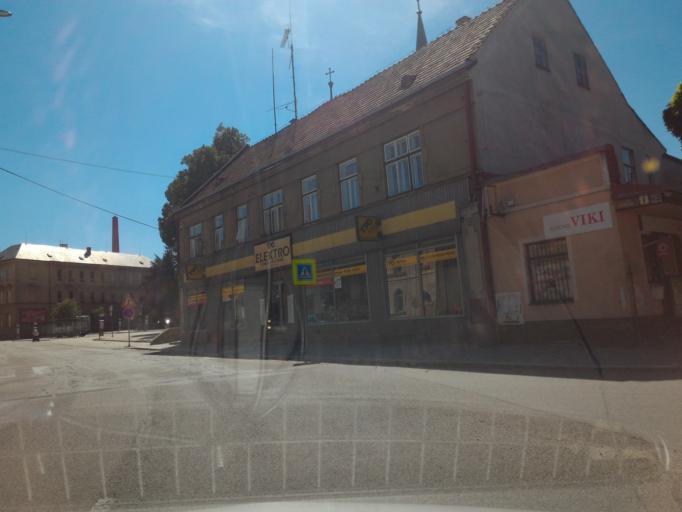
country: CZ
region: Vysocina
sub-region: Okres Jihlava
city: Trest'
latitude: 49.2927
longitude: 15.4842
